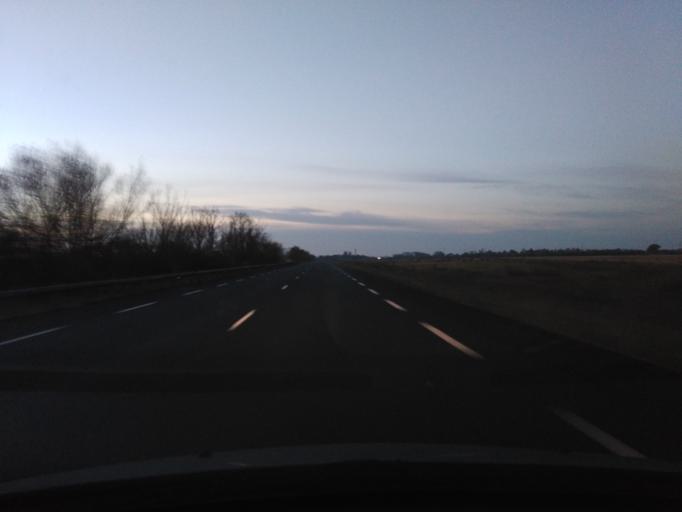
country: FR
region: Pays de la Loire
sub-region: Departement de la Vendee
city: Champagne-les-Marais
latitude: 46.3873
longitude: -1.0931
